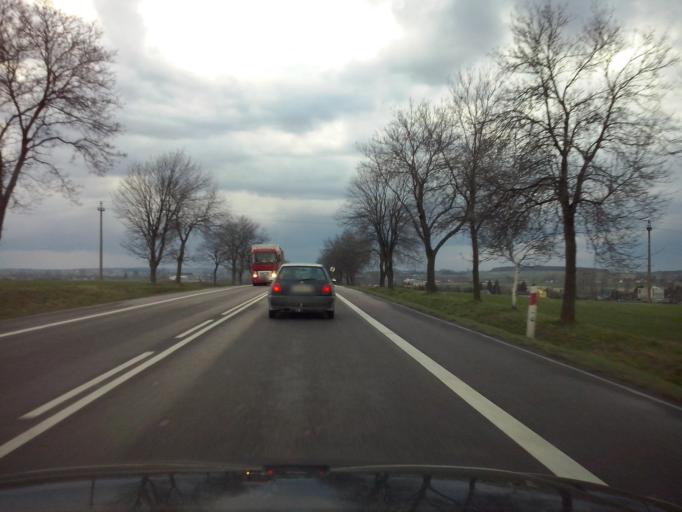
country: PL
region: Lublin Voivodeship
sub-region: Powiat chelmski
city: Rejowiec
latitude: 51.1672
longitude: 23.3589
